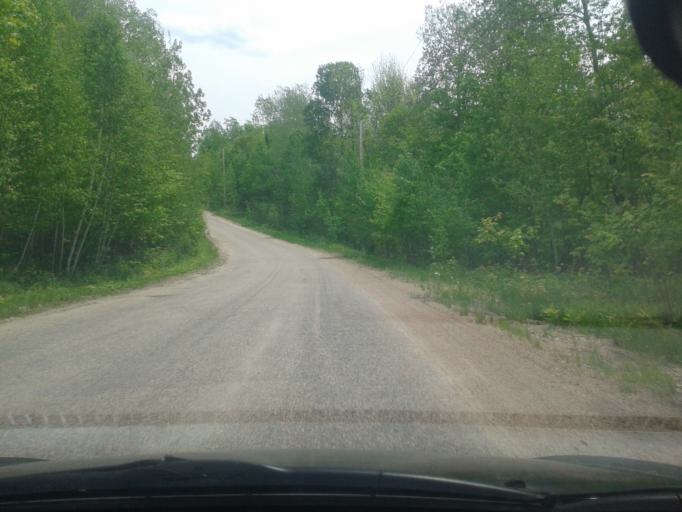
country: CA
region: Ontario
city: Powassan
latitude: 46.1855
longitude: -79.2252
